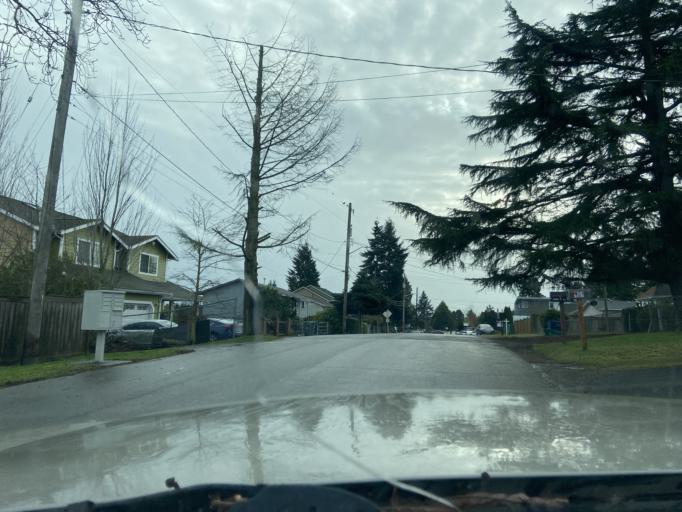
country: US
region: Washington
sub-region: King County
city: White Center
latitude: 47.5137
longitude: -122.3463
